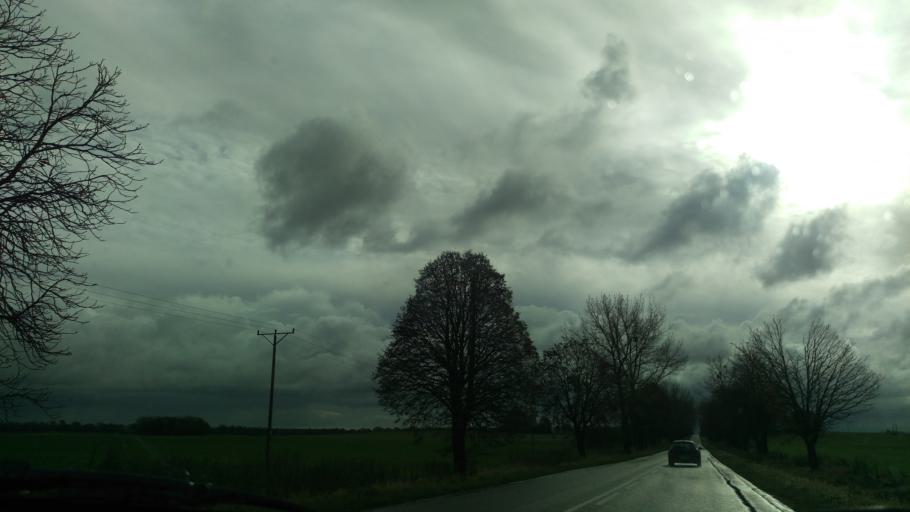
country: PL
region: West Pomeranian Voivodeship
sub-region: Powiat gryficki
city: Ploty
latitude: 53.8385
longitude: 15.2384
